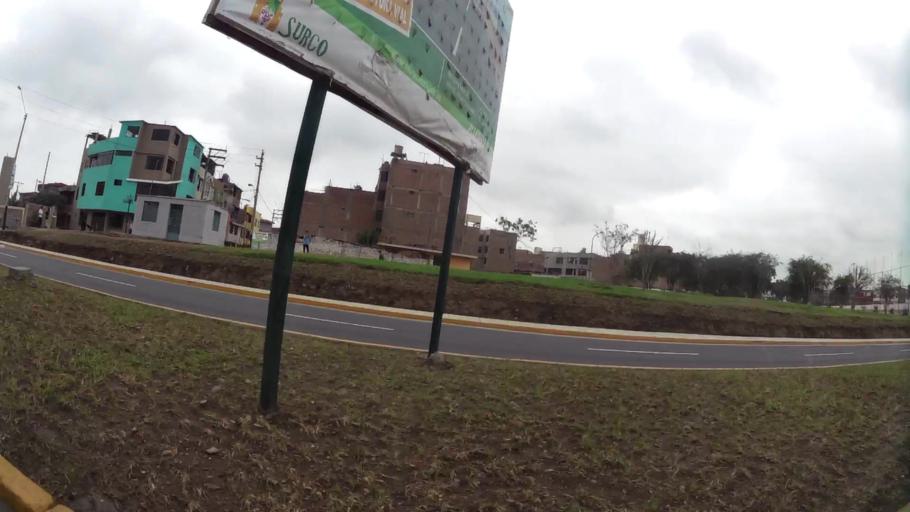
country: PE
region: Lima
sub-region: Lima
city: Surco
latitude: -12.1536
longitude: -76.9902
